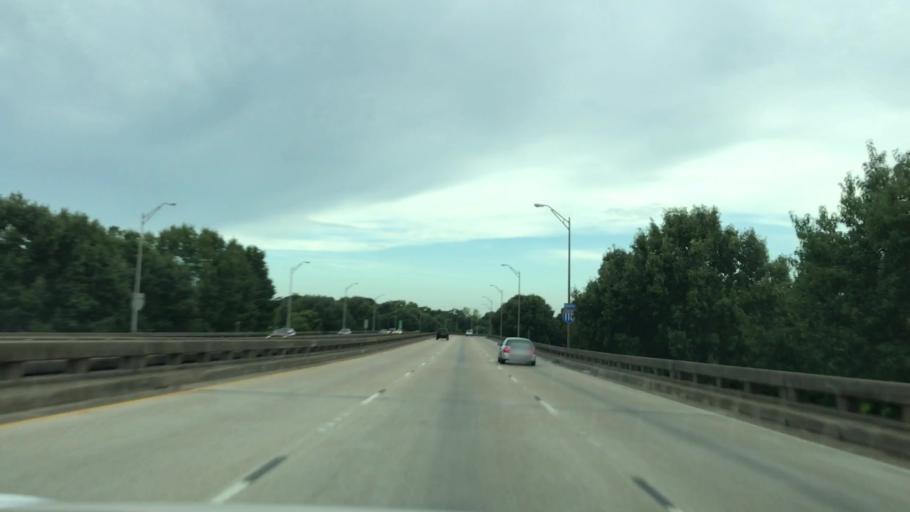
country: US
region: Louisiana
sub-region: East Baton Rouge Parish
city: Baton Rouge
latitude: 30.4844
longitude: -91.1663
